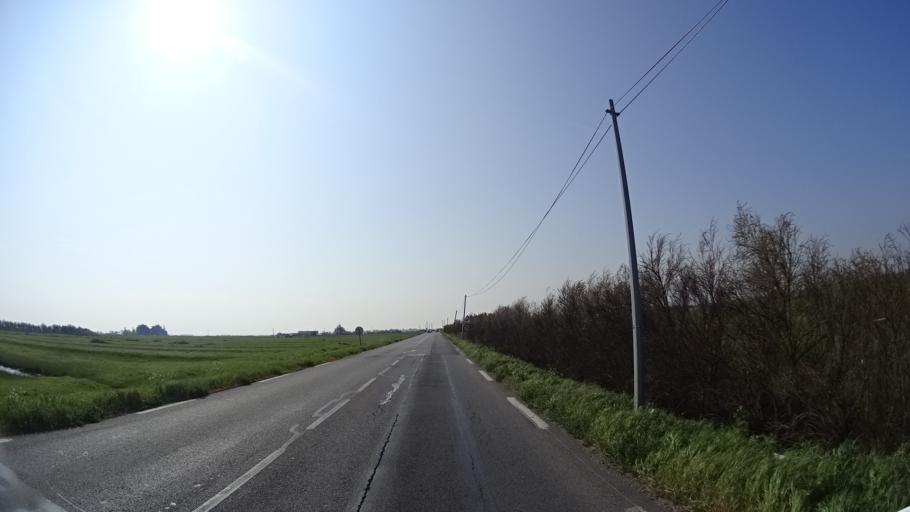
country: FR
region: Pays de la Loire
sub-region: Departement de la Loire-Atlantique
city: Bourgneuf-en-Retz
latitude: 47.0171
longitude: -1.9587
